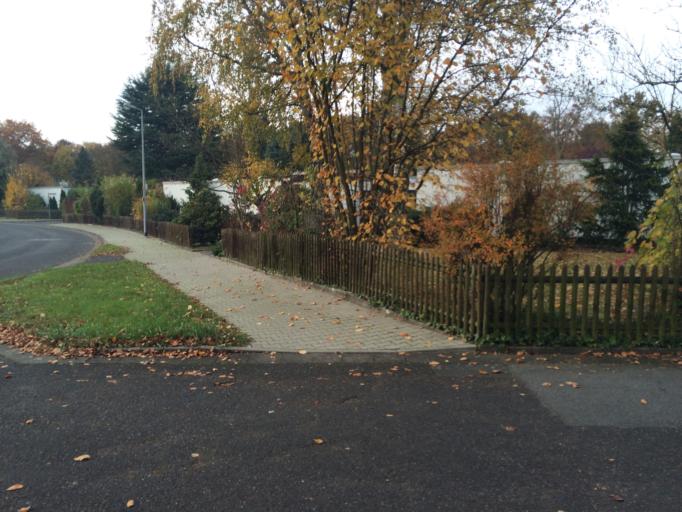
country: DE
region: Hesse
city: Morfelden-Walldorf
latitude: 50.0061
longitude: 8.5866
